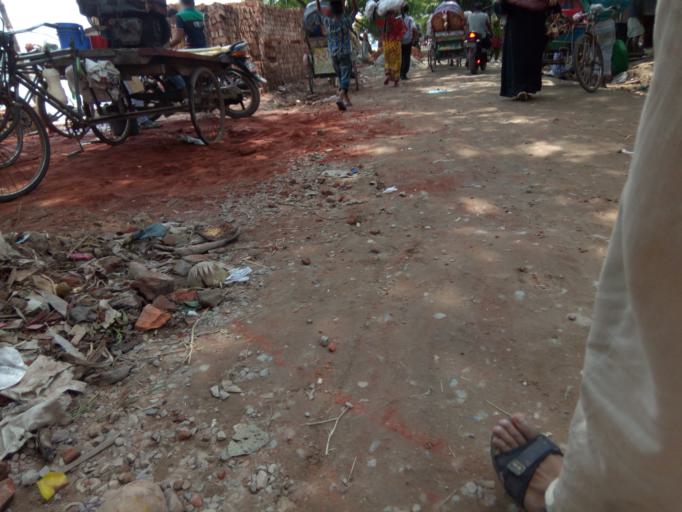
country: BD
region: Dhaka
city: Azimpur
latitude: 23.7086
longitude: 90.3784
